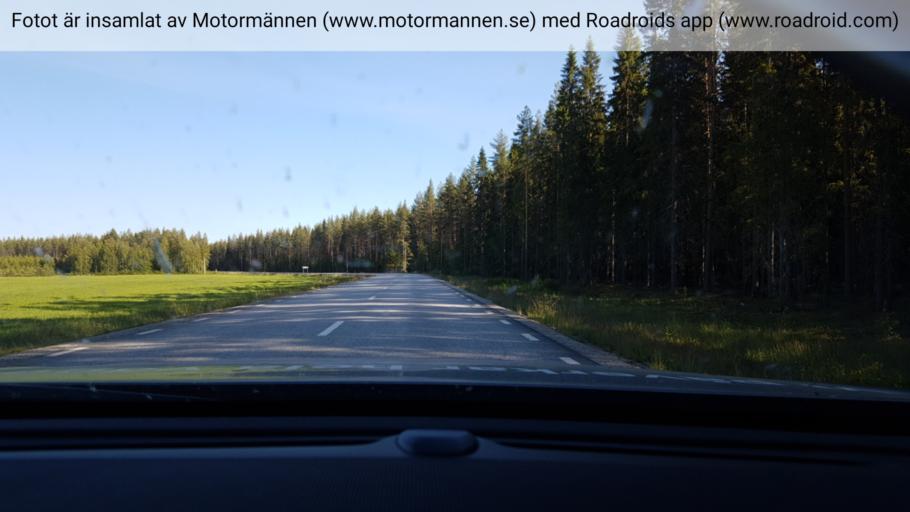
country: SE
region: Vaesterbotten
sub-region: Vindelns Kommun
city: Vindeln
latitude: 64.0934
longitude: 19.6104
